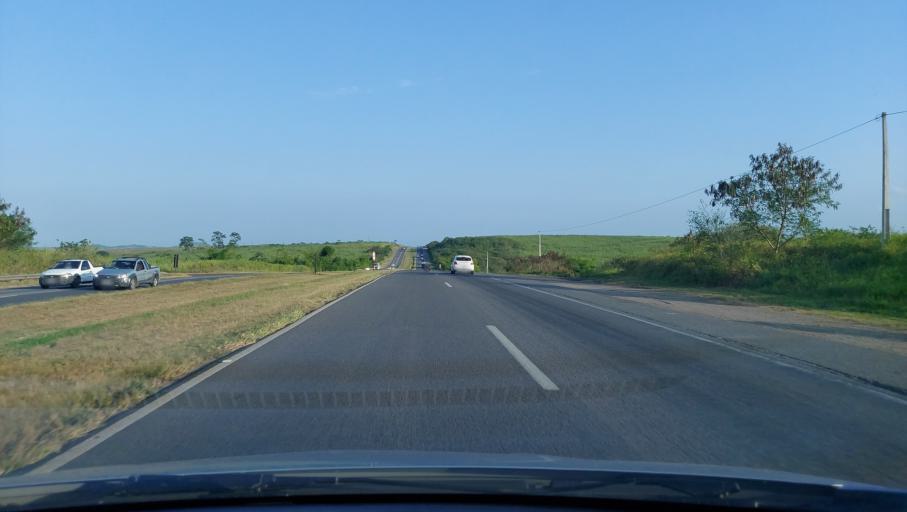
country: BR
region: Bahia
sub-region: Santo Amaro
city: Santo Amaro
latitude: -12.4642
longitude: -38.6916
